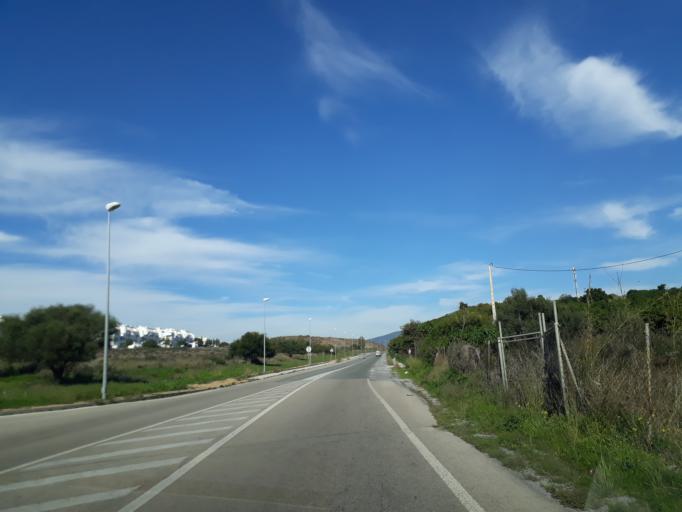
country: ES
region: Andalusia
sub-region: Provincia de Malaga
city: Fuengirola
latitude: 36.5267
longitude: -4.6858
